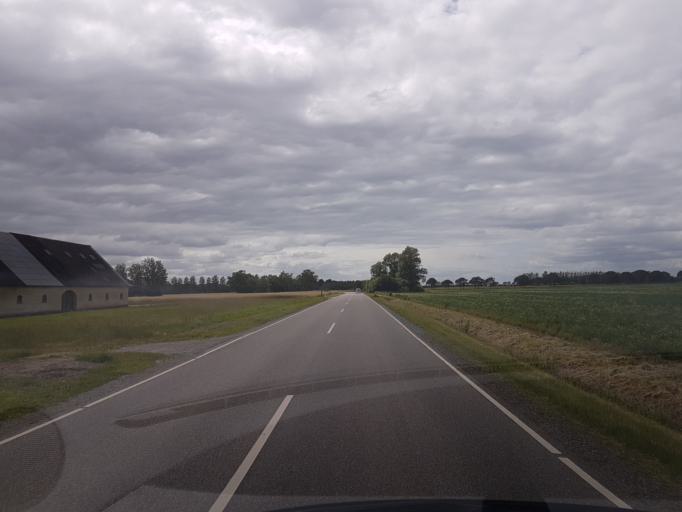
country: DK
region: South Denmark
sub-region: Nordfyns Kommune
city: Bogense
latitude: 55.5675
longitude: 10.1674
